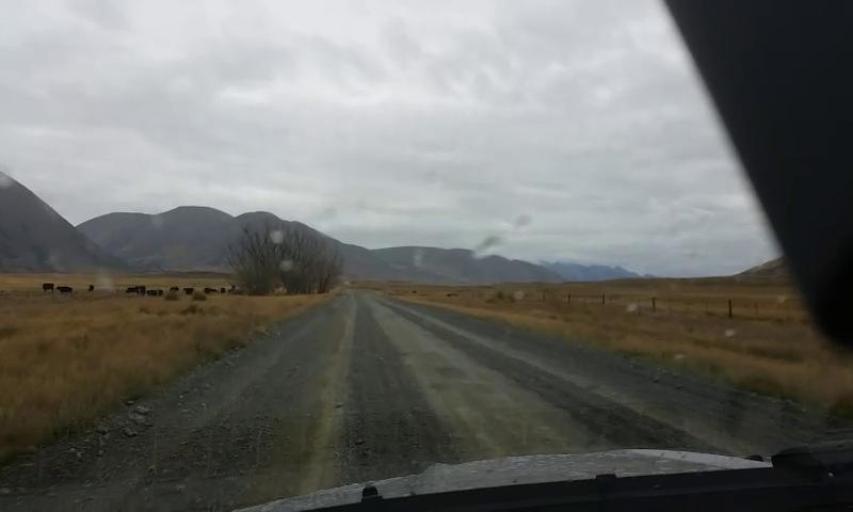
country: NZ
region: Canterbury
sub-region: Ashburton District
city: Methven
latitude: -43.6144
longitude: 171.1138
